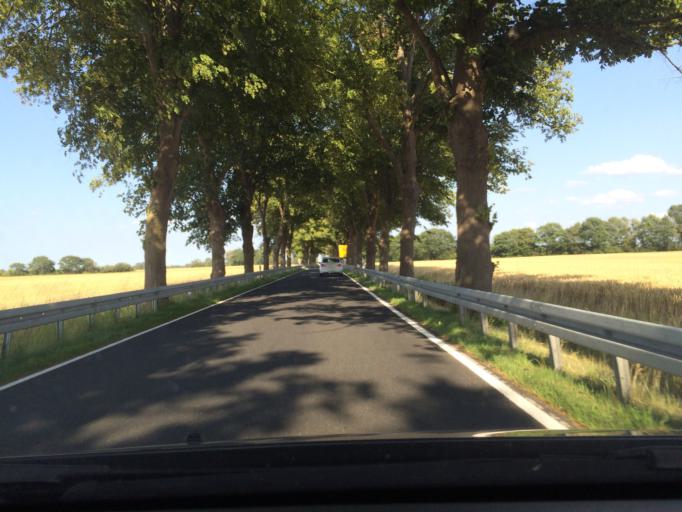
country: DE
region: Mecklenburg-Vorpommern
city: Niepars
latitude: 54.3339
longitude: 12.8752
